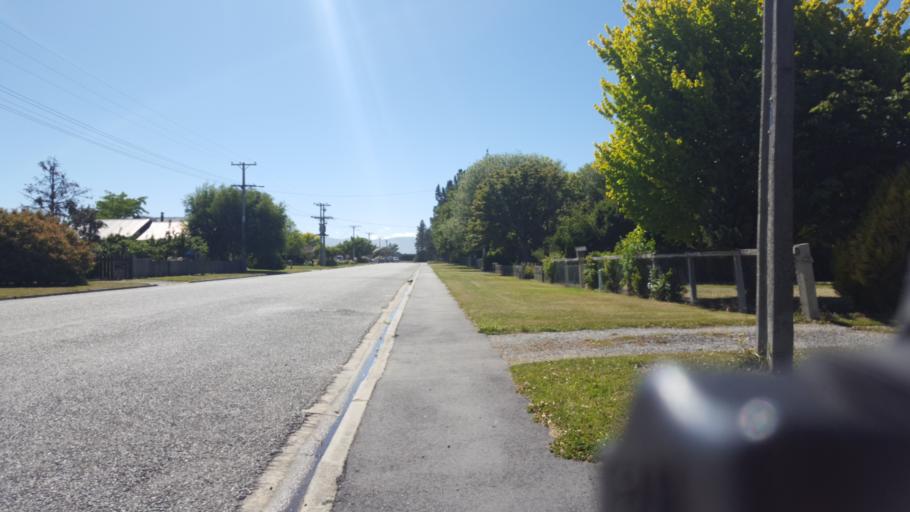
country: NZ
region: Otago
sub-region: Dunedin City
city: Dunedin
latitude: -45.1237
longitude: 170.0972
